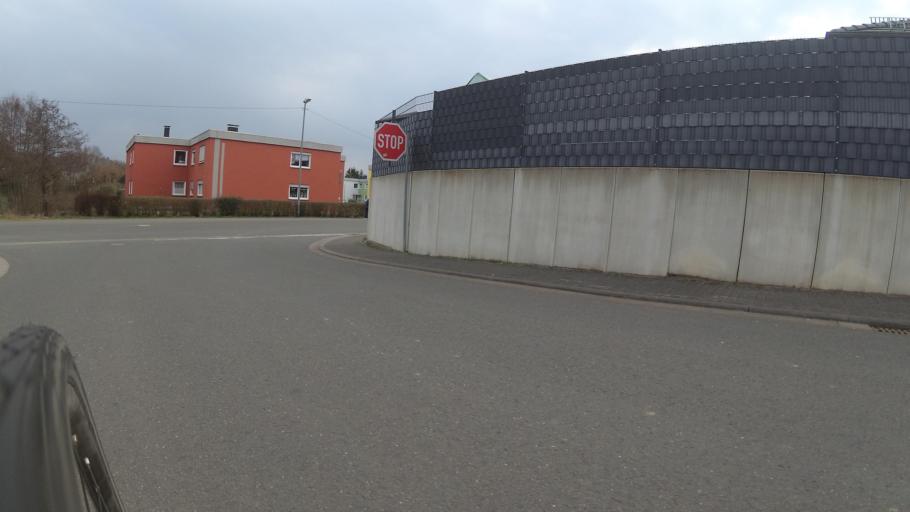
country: DE
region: Rheinland-Pfalz
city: Birkenfeld
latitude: 49.6560
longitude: 7.1695
